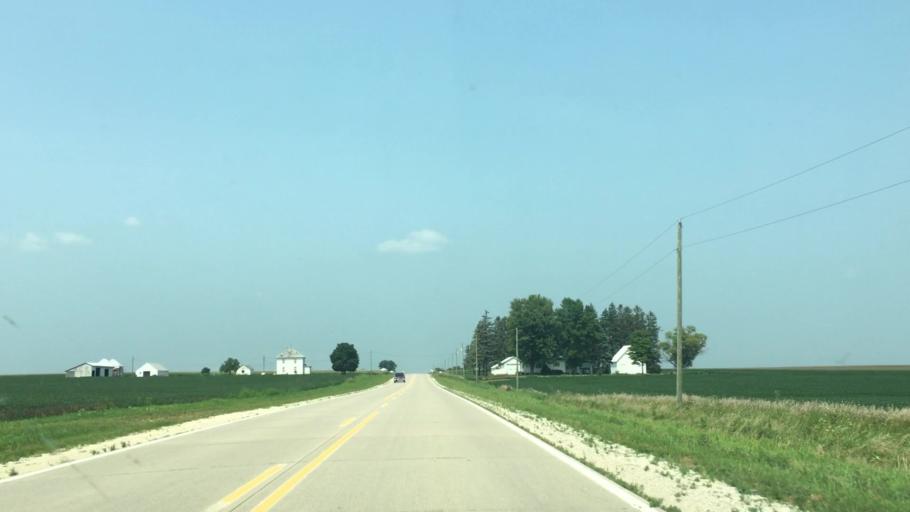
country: US
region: Iowa
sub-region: Fayette County
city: Oelwein
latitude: 42.7086
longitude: -91.8048
